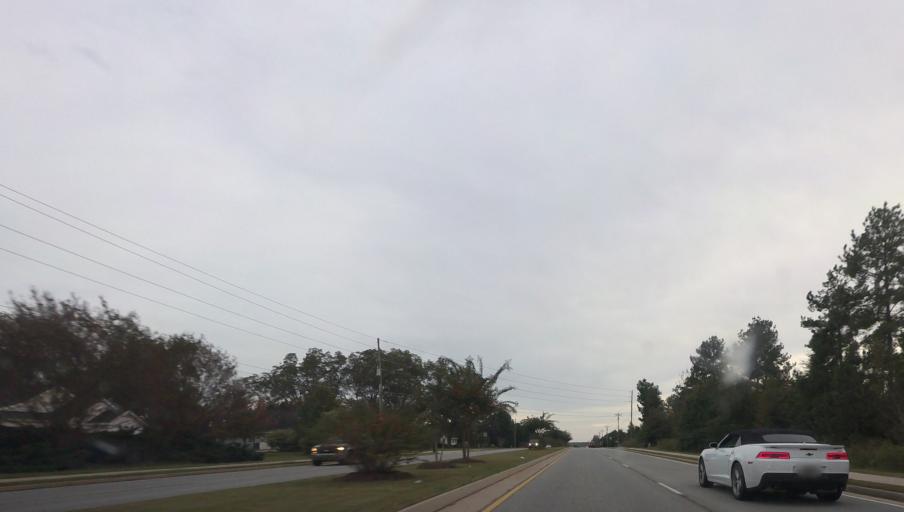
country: US
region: Georgia
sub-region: Houston County
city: Perry
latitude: 32.5159
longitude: -83.6625
